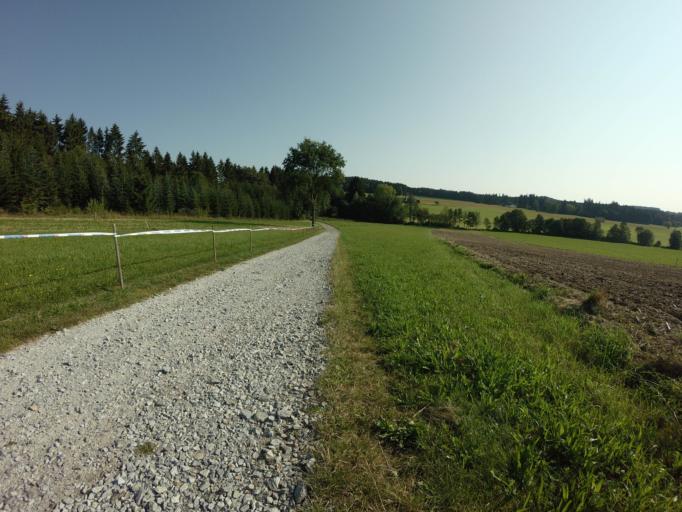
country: AT
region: Upper Austria
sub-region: Politischer Bezirk Urfahr-Umgebung
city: Bad Leonfelden
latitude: 48.5309
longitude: 14.3079
